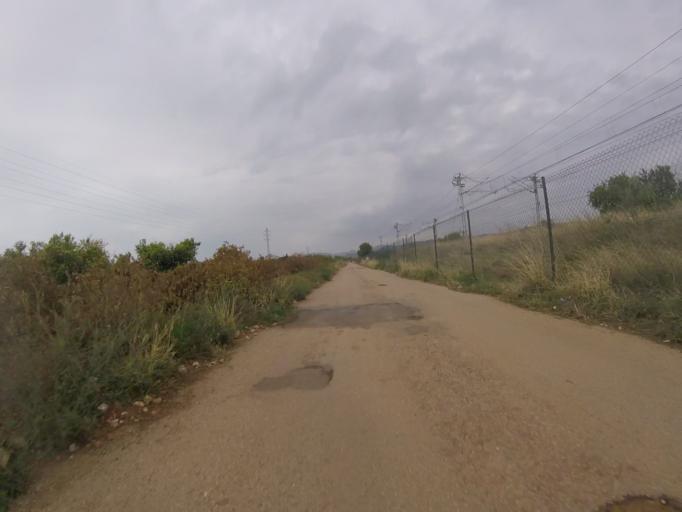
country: ES
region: Valencia
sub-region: Provincia de Castello
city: Torreblanca
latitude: 40.2173
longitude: 0.2048
